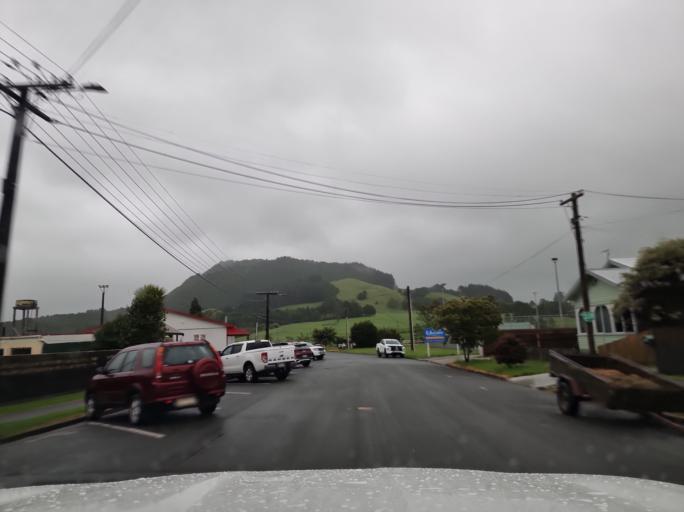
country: NZ
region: Northland
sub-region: Whangarei
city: Whangarei
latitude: -35.6015
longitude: 174.2855
